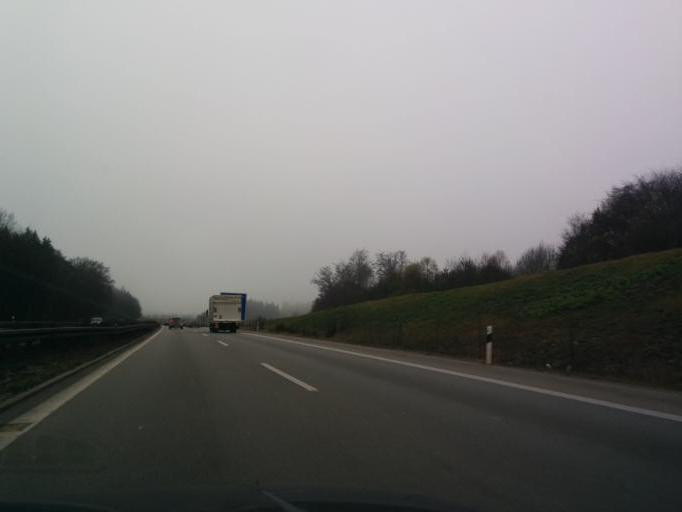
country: DE
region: Bavaria
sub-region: Upper Bavaria
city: Wessling
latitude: 48.0910
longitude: 11.2360
